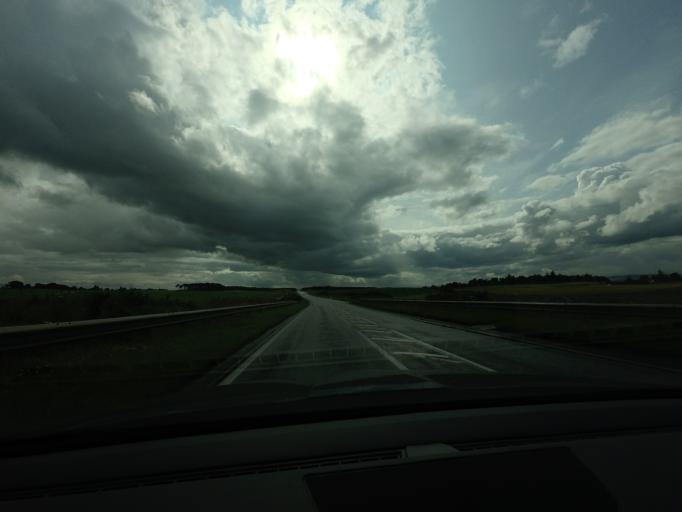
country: GB
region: Scotland
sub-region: Highland
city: Nairn
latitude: 57.5542
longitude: -3.9781
